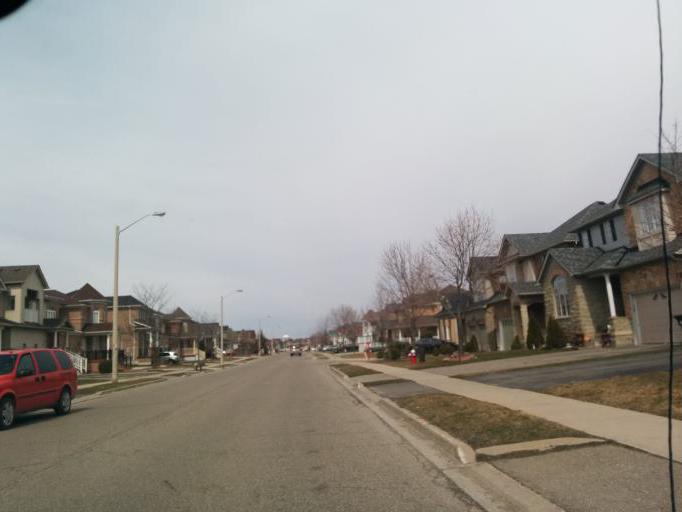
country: CA
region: Ontario
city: Brampton
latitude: 43.7137
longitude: -79.8180
